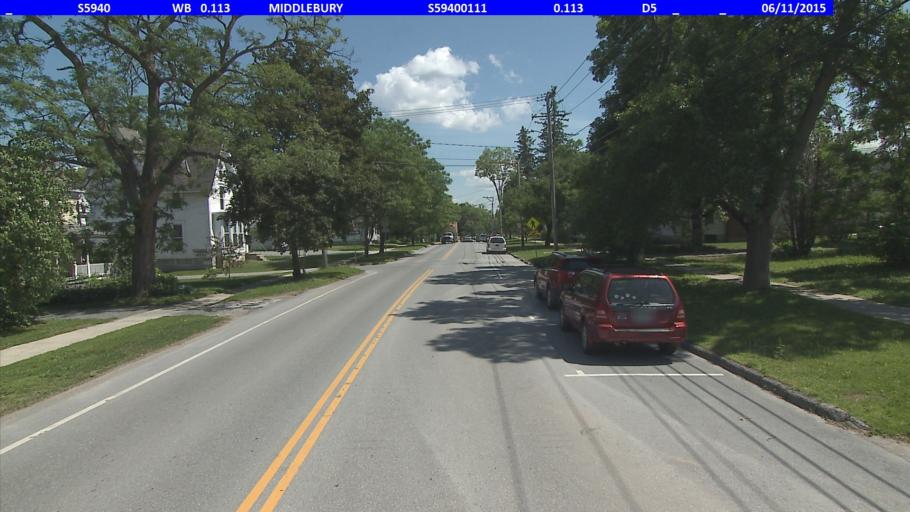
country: US
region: Vermont
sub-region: Addison County
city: Middlebury (village)
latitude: 44.0127
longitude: -73.1729
